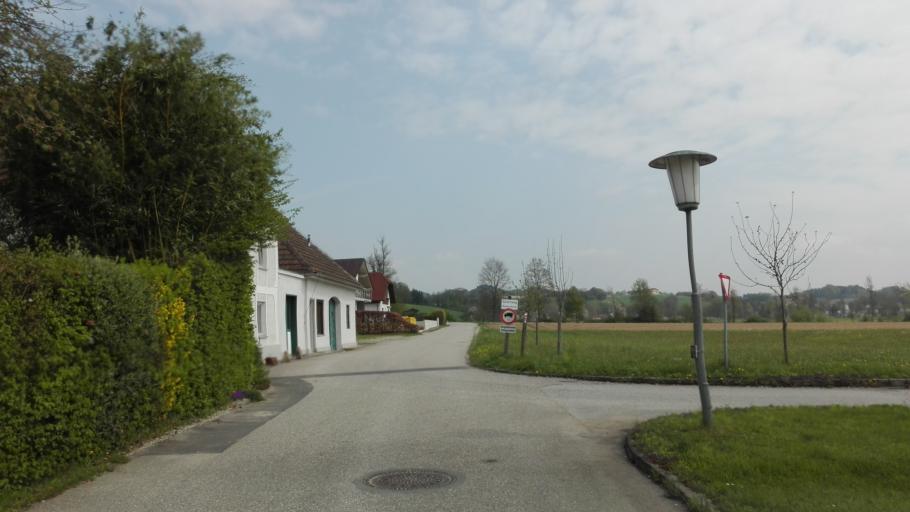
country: AT
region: Upper Austria
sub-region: Politischer Bezirk Perg
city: Bad Kreuzen
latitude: 48.2239
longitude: 14.7254
